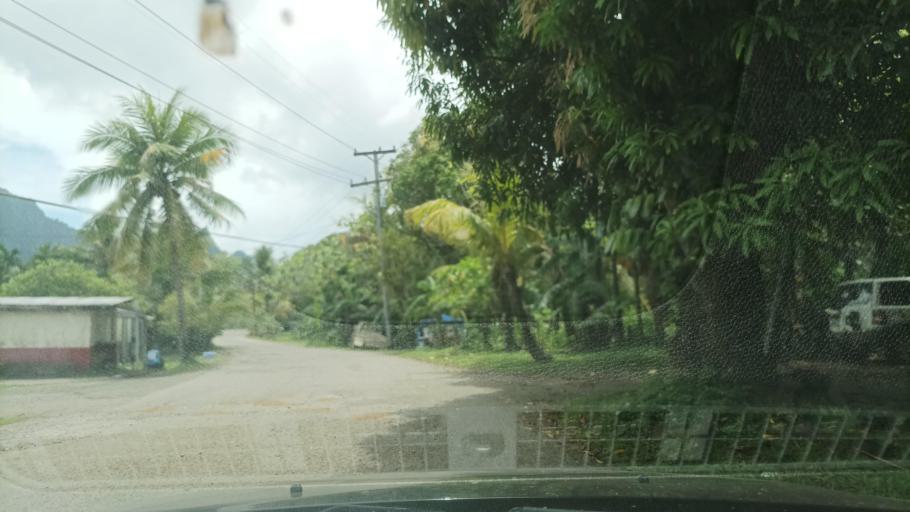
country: FM
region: Kosrae
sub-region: Lelu Municipality
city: Lelu
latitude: 5.3375
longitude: 163.0127
